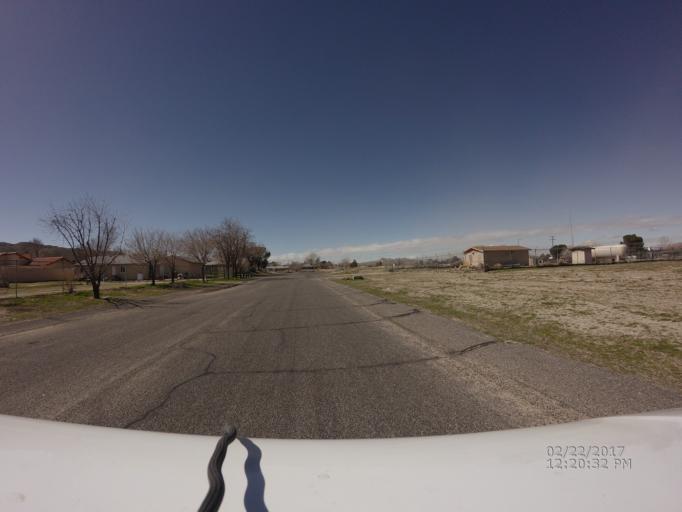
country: US
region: California
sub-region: Los Angeles County
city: Lake Los Angeles
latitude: 34.6157
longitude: -117.8340
